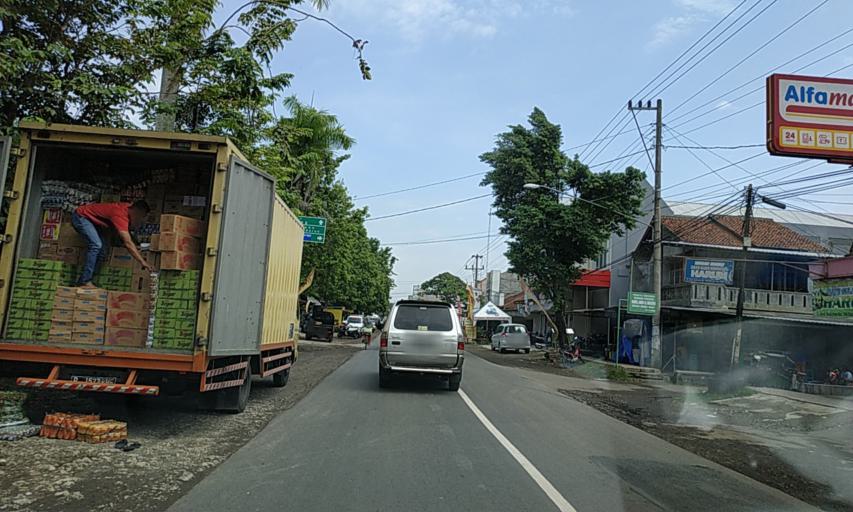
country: ID
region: Central Java
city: Sidareja
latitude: -7.4853
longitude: 108.7933
